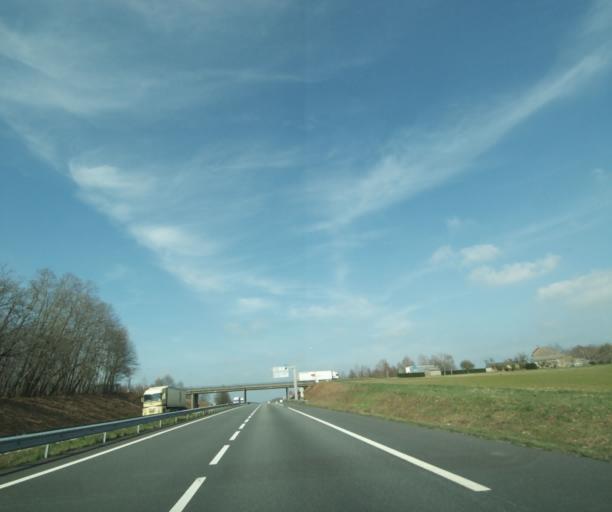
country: FR
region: Limousin
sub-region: Departement de la Creuse
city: Saint-Maurice-la-Souterraine
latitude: 46.2025
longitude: 1.3825
